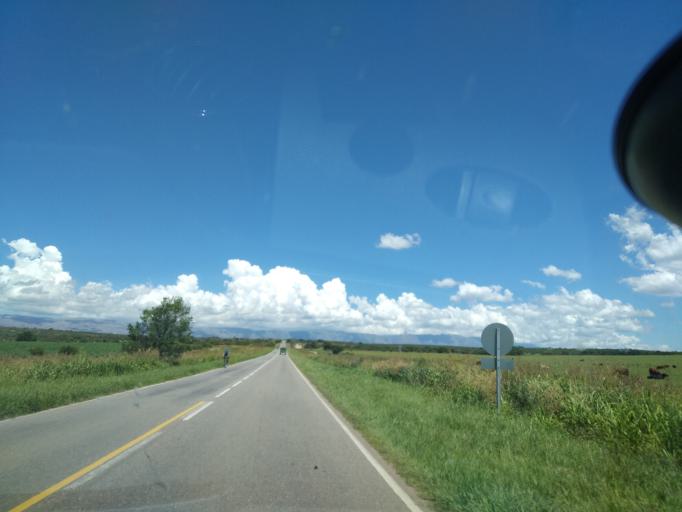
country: AR
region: Cordoba
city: Villa Cura Brochero
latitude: -31.6795
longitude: -65.0844
